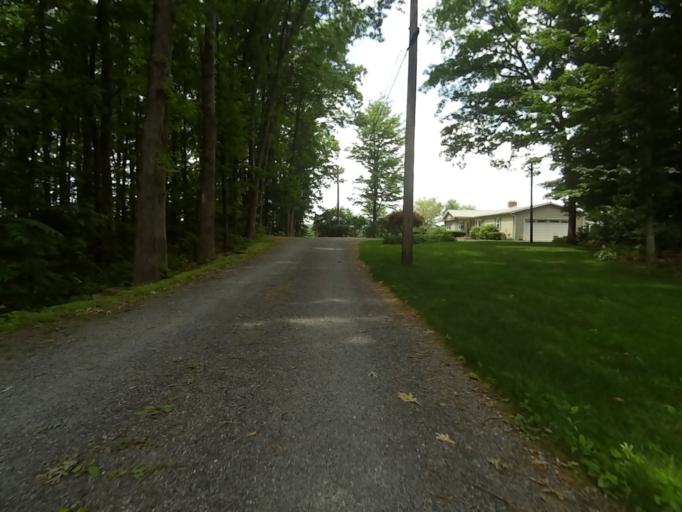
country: US
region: Pennsylvania
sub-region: Centre County
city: Park Forest Village
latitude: 40.8145
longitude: -77.9007
